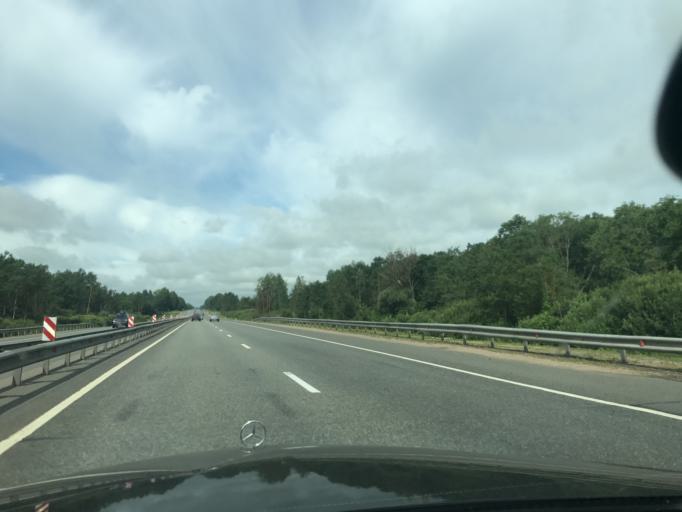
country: RU
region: Smolensk
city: Yartsevo
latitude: 55.0594
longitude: 32.5826
